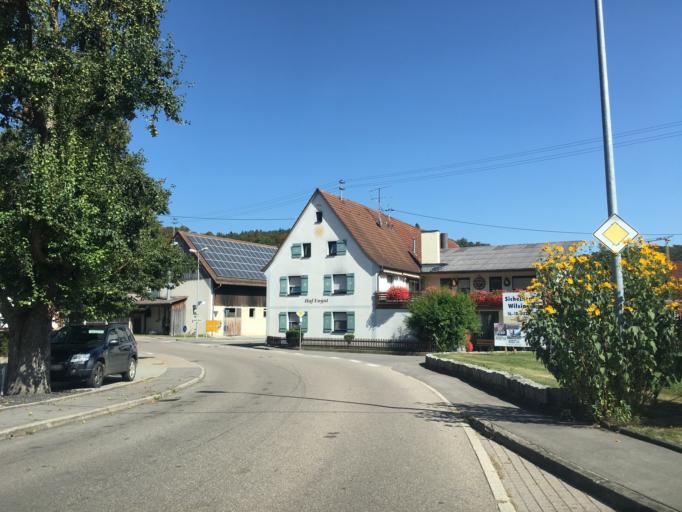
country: DE
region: Baden-Wuerttemberg
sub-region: Tuebingen Region
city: Hayingen
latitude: 48.2929
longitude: 9.4921
